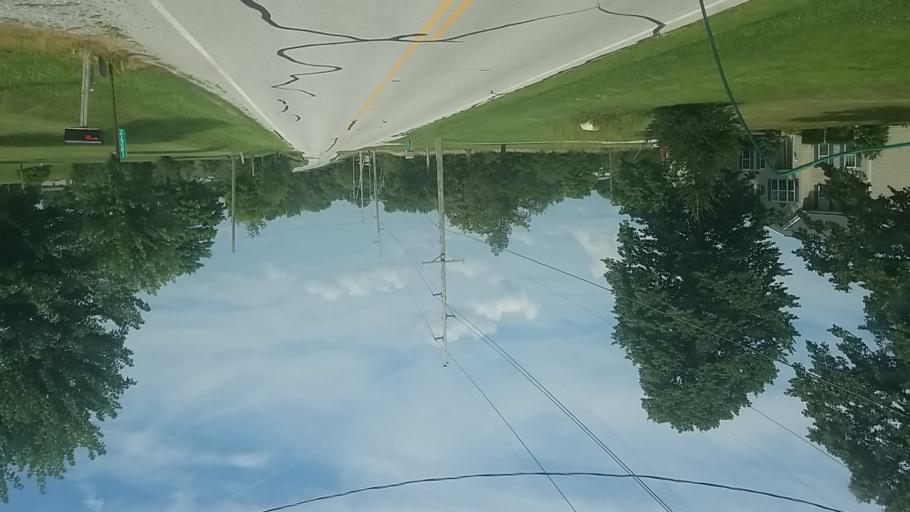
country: US
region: Ohio
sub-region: Hardin County
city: Forest
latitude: 40.7818
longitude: -83.5323
